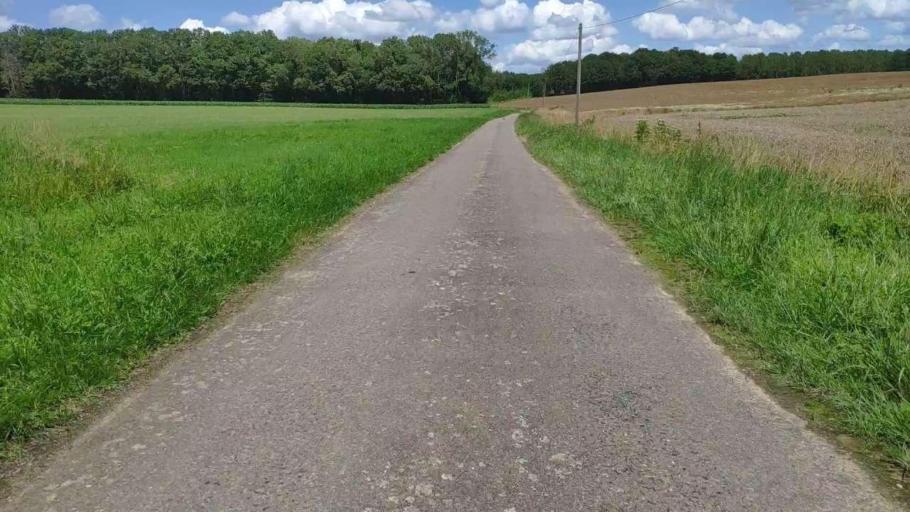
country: FR
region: Franche-Comte
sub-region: Departement du Jura
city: Chaussin
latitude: 46.8689
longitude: 5.4592
